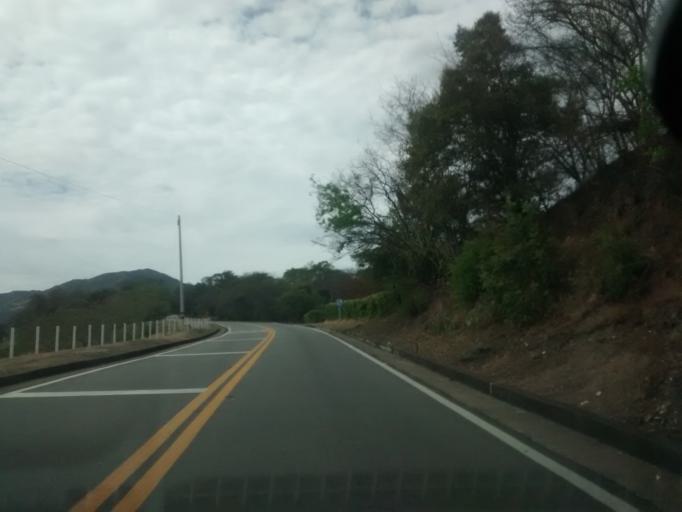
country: CO
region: Cundinamarca
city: Agua de Dios
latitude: 4.4125
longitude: -74.7092
